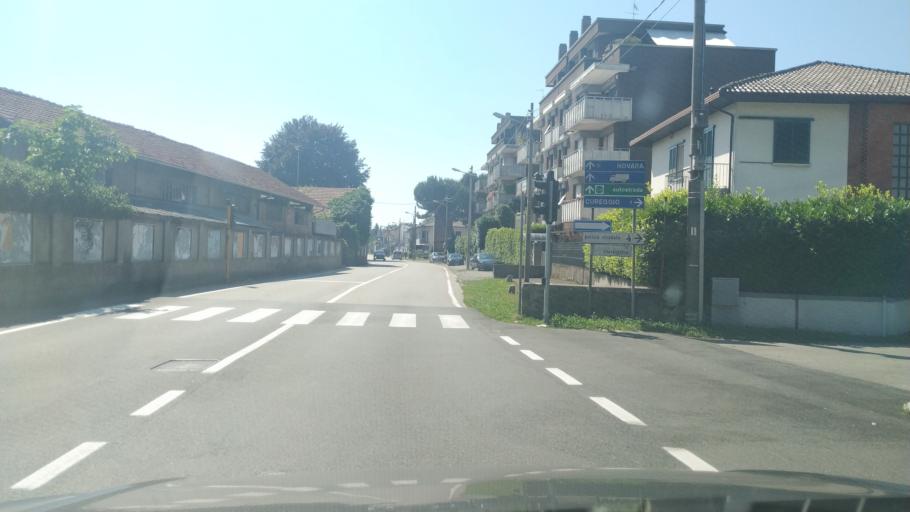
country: IT
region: Piedmont
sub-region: Provincia di Novara
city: Borgomanero
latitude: 45.6944
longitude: 8.4613
